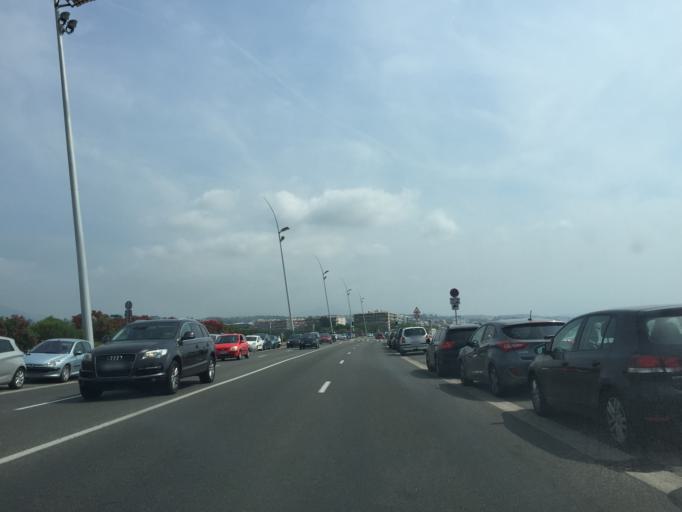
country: FR
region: Provence-Alpes-Cote d'Azur
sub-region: Departement des Alpes-Maritimes
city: Cagnes-sur-Mer
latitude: 43.6472
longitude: 7.1482
